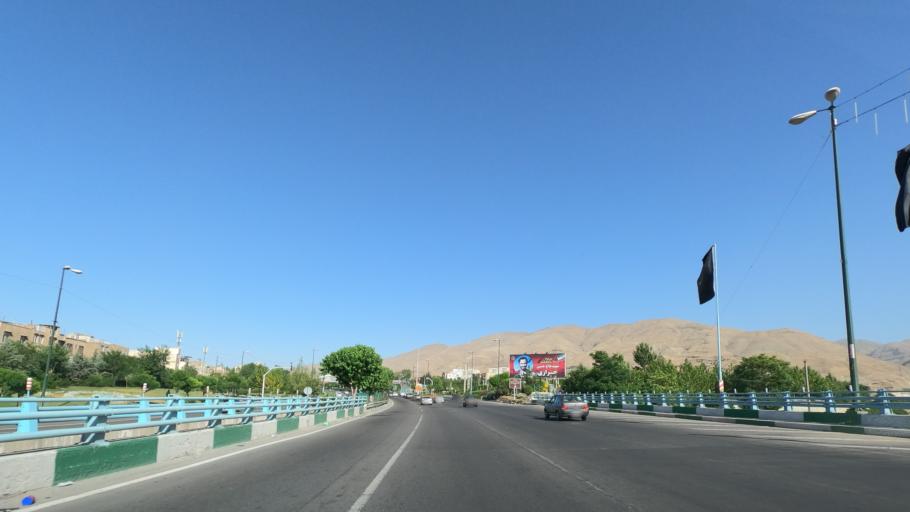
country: IR
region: Tehran
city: Shahr-e Qods
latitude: 35.7566
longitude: 51.2678
